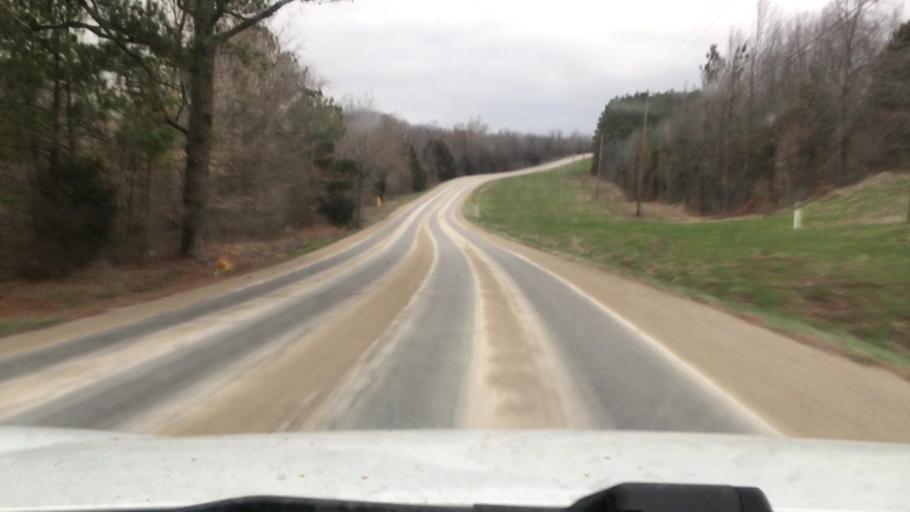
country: US
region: Missouri
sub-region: Saint Charles County
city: Weldon Spring
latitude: 38.6713
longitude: -90.7321
